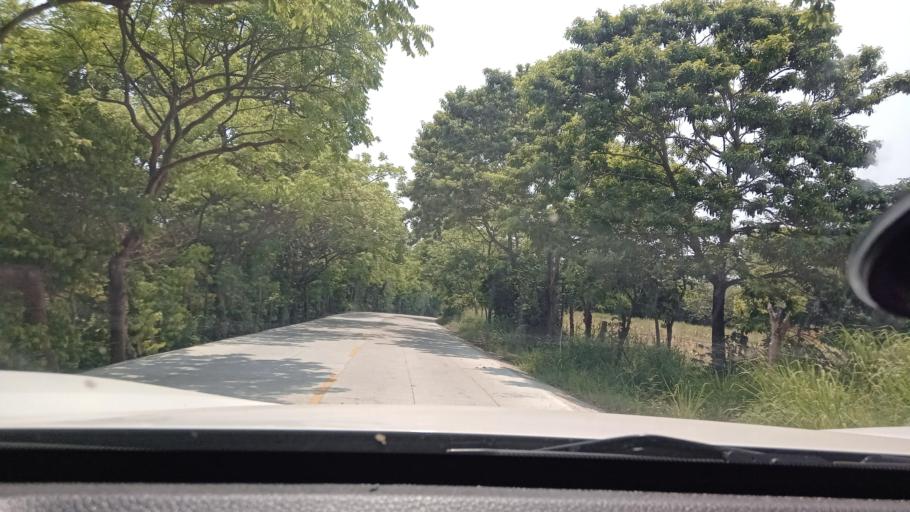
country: MX
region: Veracruz
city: Catemaco
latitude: 18.5562
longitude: -95.0014
